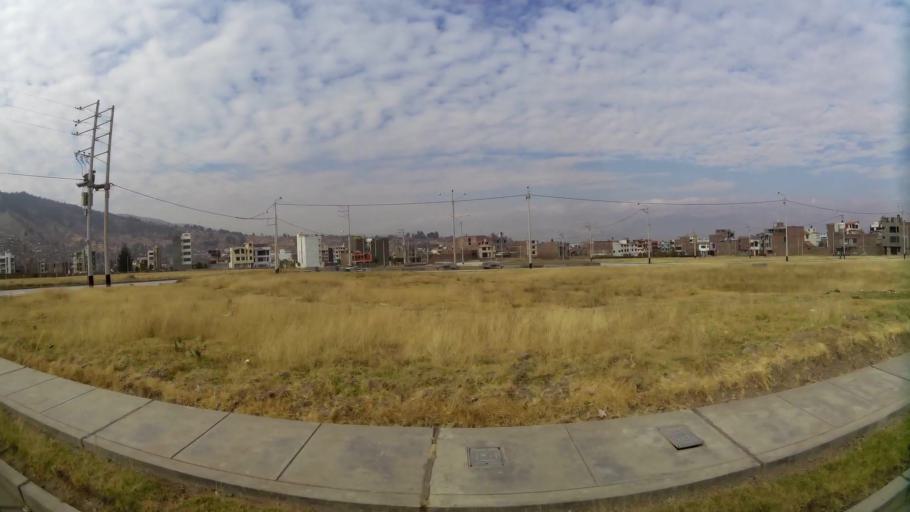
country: PE
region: Junin
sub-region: Provincia de Huancayo
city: Huancayo
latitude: -12.0463
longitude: -75.1907
